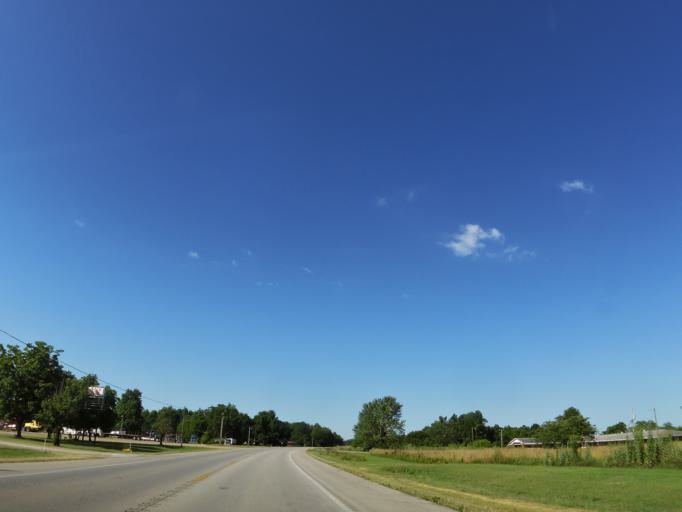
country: US
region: Arkansas
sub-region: Clay County
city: Corning
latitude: 36.5470
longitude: -90.5221
